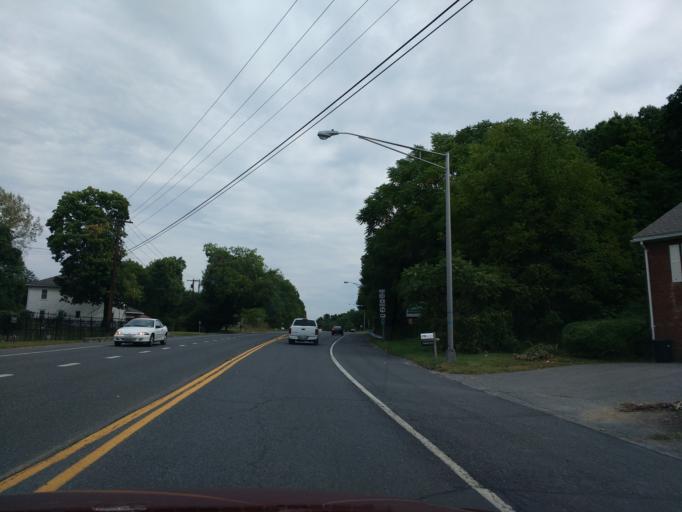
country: US
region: New York
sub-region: Ulster County
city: Lincoln Park
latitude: 41.9426
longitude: -73.9861
